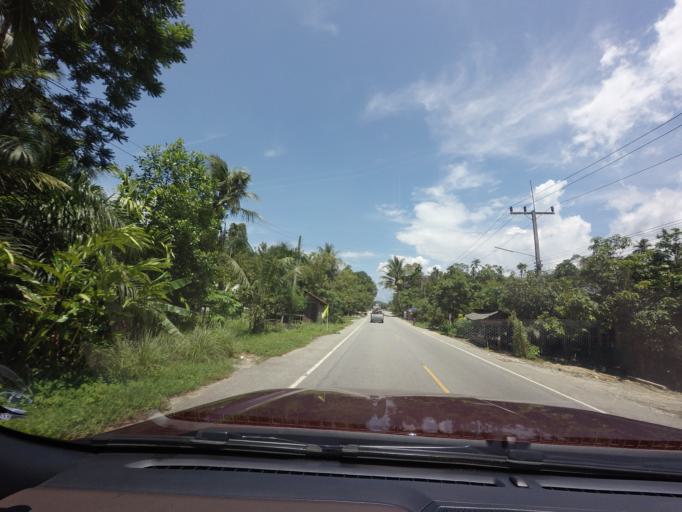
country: TH
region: Narathiwat
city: Chanae
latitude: 6.1343
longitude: 101.6989
